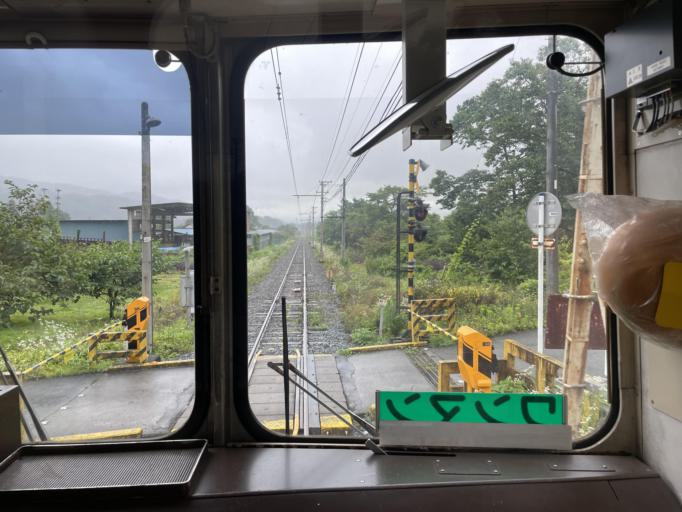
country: JP
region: Saitama
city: Chichibu
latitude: 35.9535
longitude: 139.0283
